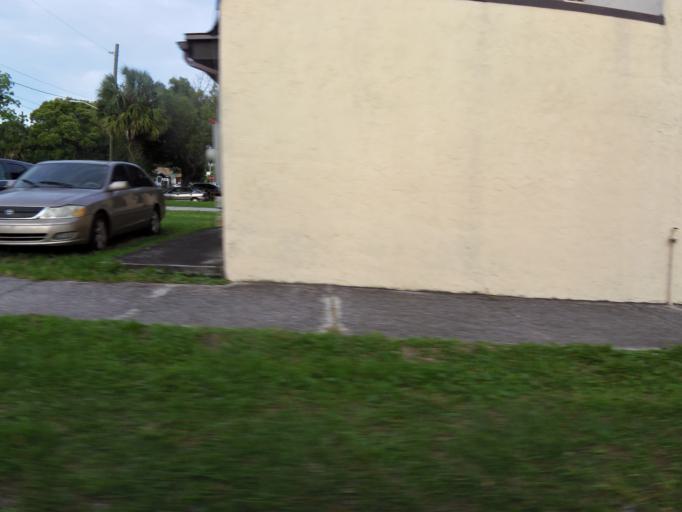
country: US
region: Florida
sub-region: Duval County
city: Jacksonville
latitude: 30.3462
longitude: -81.6431
